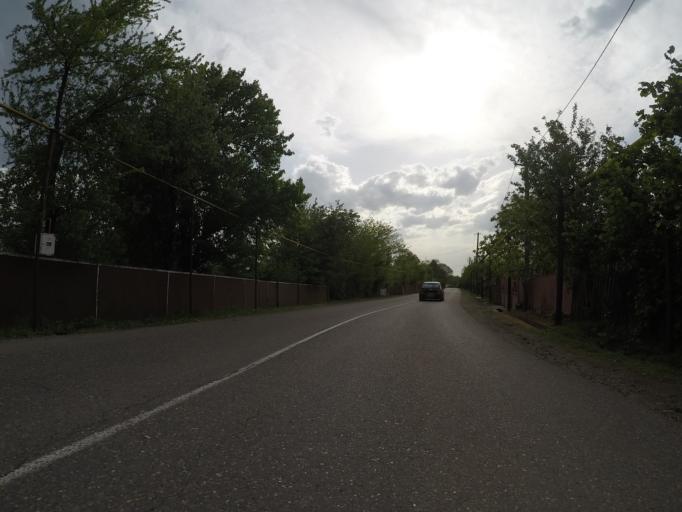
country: GE
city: Shorapani
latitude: 42.1468
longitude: 43.1036
